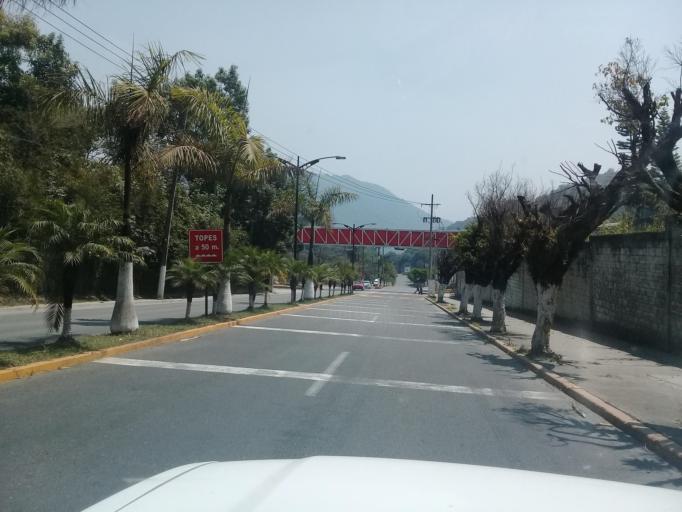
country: MX
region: Veracruz
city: Ixtac Zoquitlan
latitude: 18.8610
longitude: -97.0403
